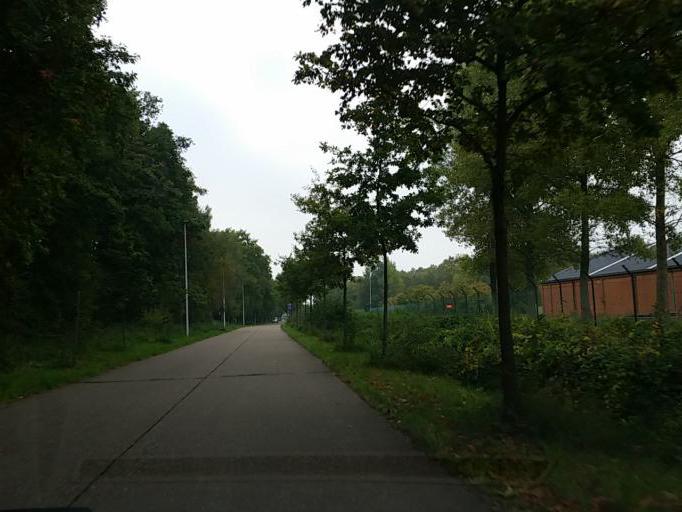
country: BE
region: Flanders
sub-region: Provincie Antwerpen
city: Brasschaat
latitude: 51.3310
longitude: 4.5051
